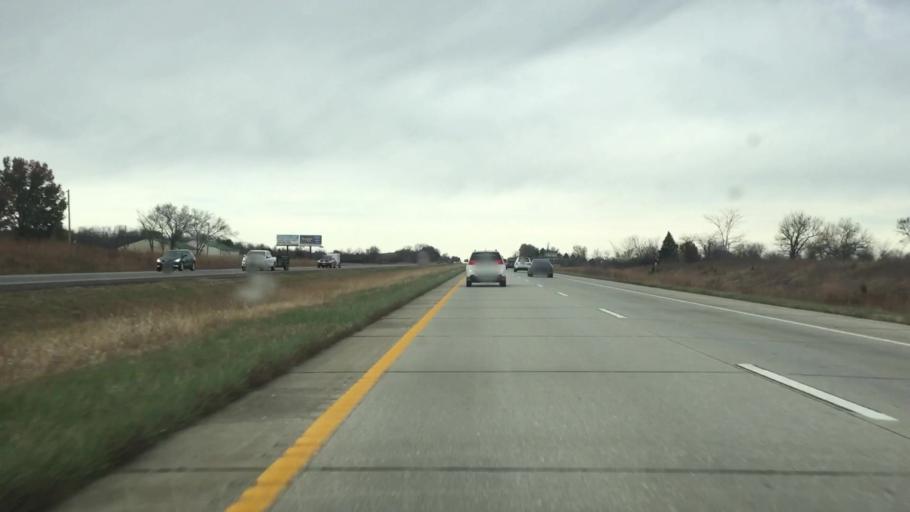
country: US
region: Missouri
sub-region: Saint Clair County
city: Osceola
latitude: 38.0913
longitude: -93.7076
